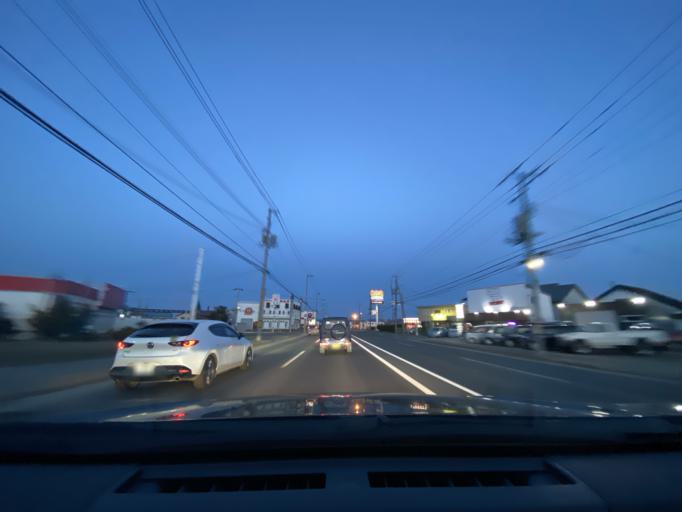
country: JP
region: Hokkaido
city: Kitami
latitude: 43.7988
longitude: 143.8311
